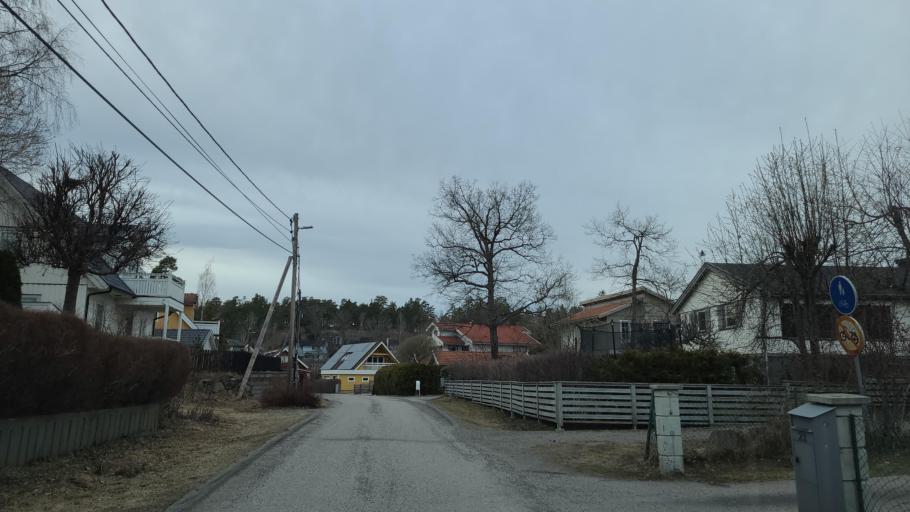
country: SE
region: Stockholm
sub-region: Nacka Kommun
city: Boo
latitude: 59.3187
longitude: 18.2631
